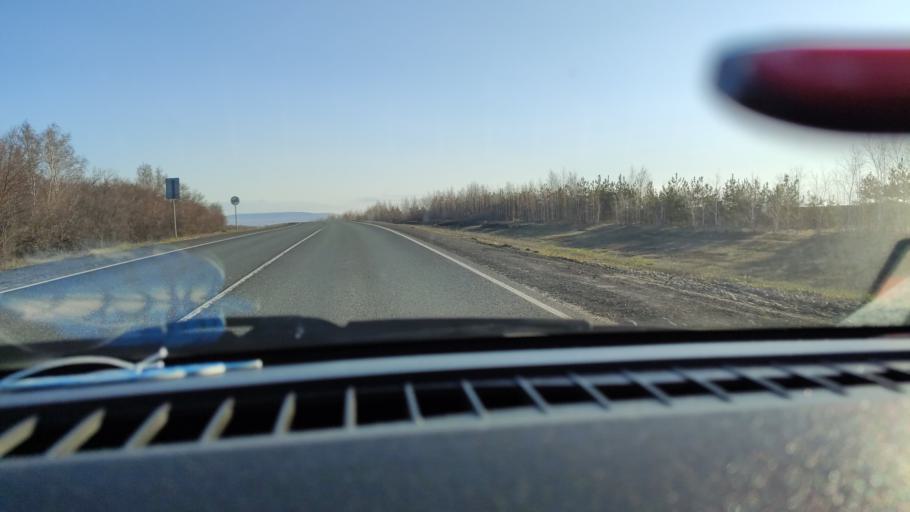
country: RU
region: Saratov
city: Balakovo
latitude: 52.1626
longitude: 47.8233
